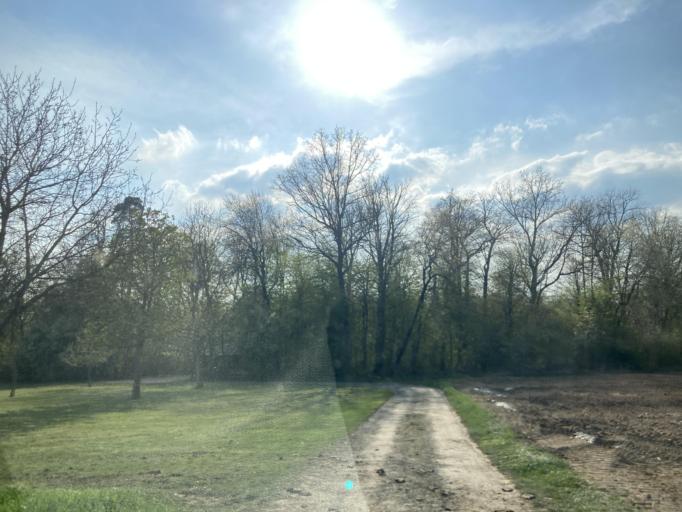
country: DE
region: Baden-Wuerttemberg
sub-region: Tuebingen Region
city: Gomaringen
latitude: 48.4939
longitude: 9.0842
